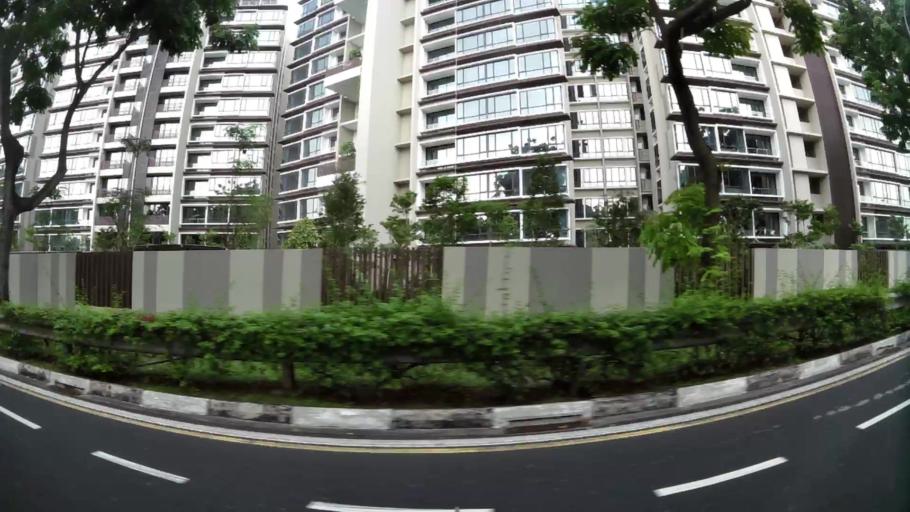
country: SG
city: Singapore
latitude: 1.3682
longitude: 103.9455
